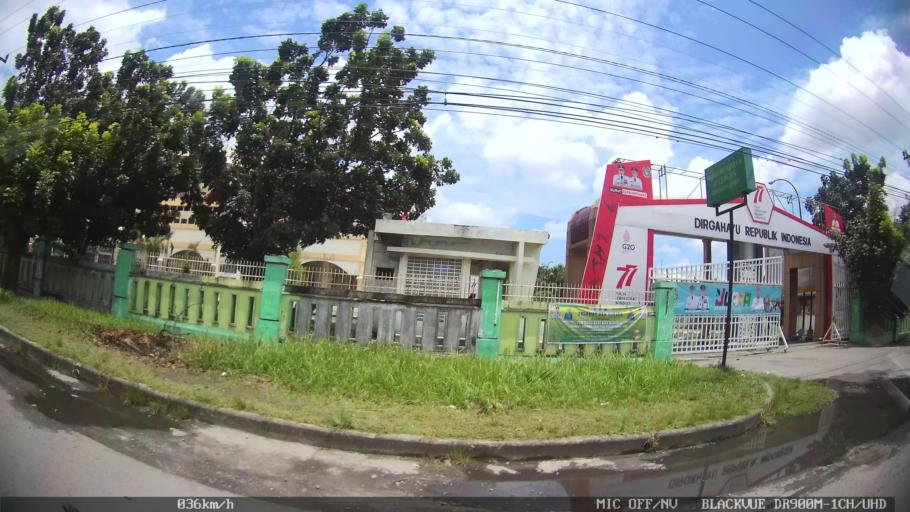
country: ID
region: North Sumatra
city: Medan
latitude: 3.6064
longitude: 98.7083
